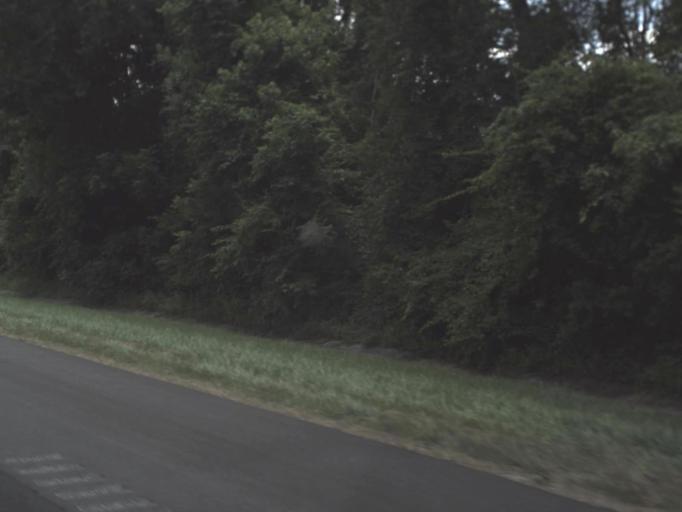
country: US
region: Florida
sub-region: Madison County
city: Madison
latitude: 30.4233
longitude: -83.4450
